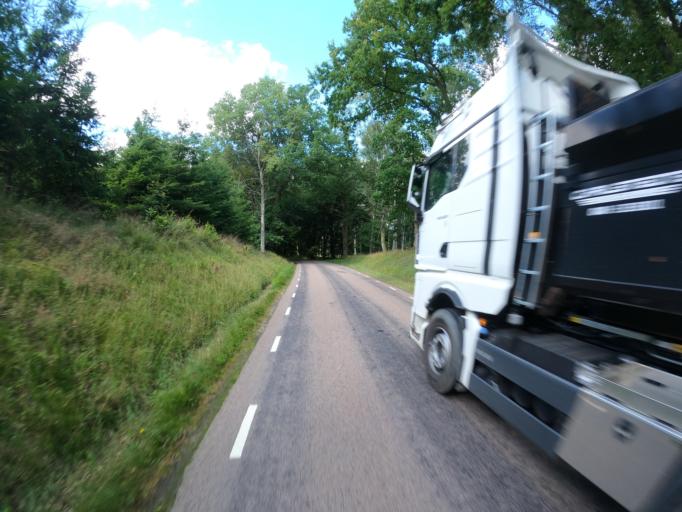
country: SE
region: Skane
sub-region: Lunds Kommun
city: Veberod
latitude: 55.5799
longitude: 13.4687
